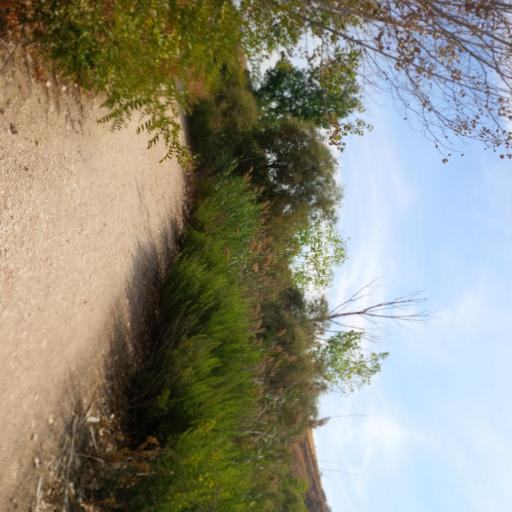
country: ES
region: Madrid
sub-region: Provincia de Madrid
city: Mejorada del Campo
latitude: 40.4134
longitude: -3.4895
